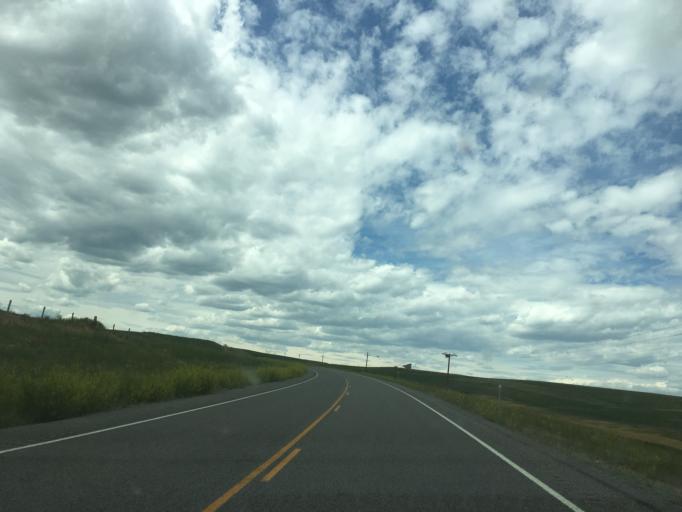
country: US
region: Montana
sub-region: Teton County
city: Choteau
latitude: 48.1362
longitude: -112.3924
